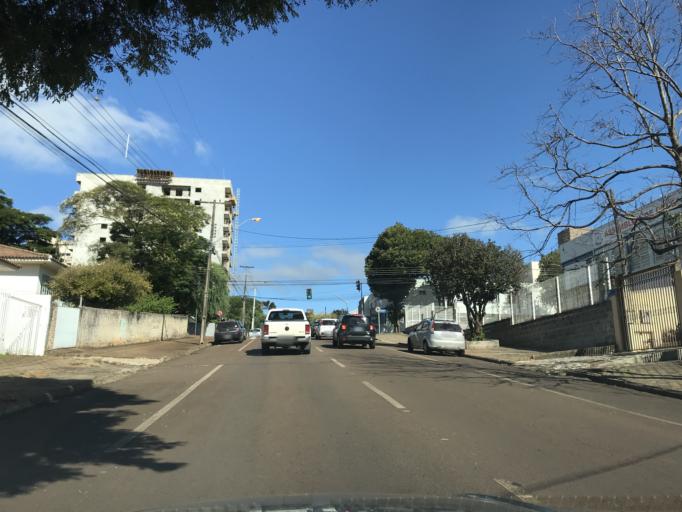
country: BR
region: Parana
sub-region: Cascavel
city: Cascavel
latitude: -24.9496
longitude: -53.4690
